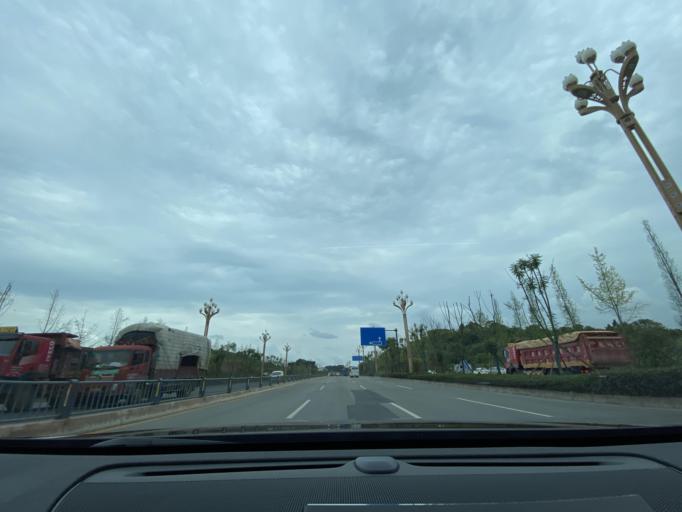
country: CN
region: Sichuan
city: Jiancheng
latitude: 30.4771
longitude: 104.4881
